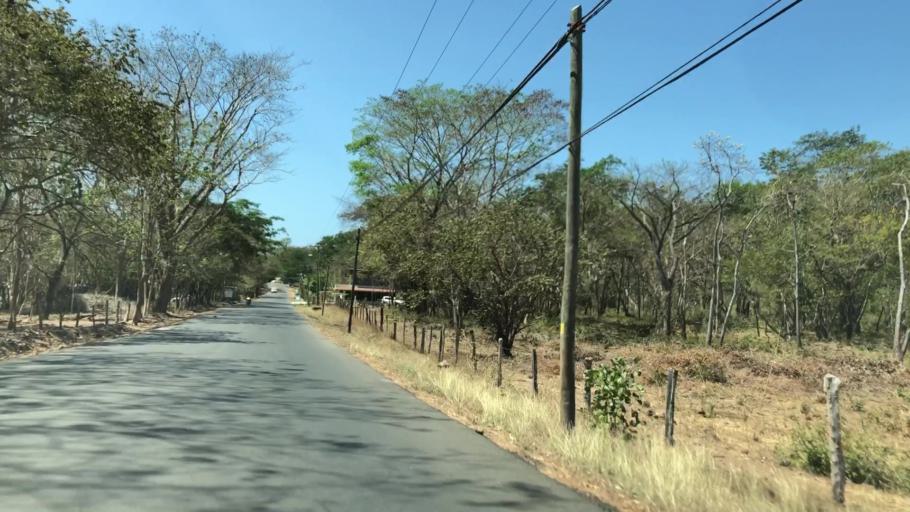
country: CR
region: Guanacaste
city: Sardinal
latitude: 10.3441
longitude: -85.8433
